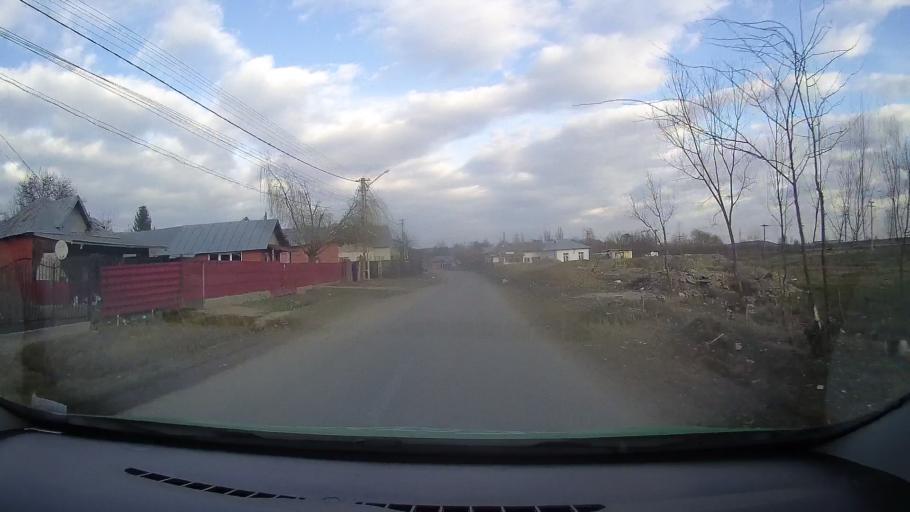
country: RO
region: Dambovita
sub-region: Comuna Gura Ocnitei
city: Gura Ocnitei
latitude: 44.9386
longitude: 25.5753
